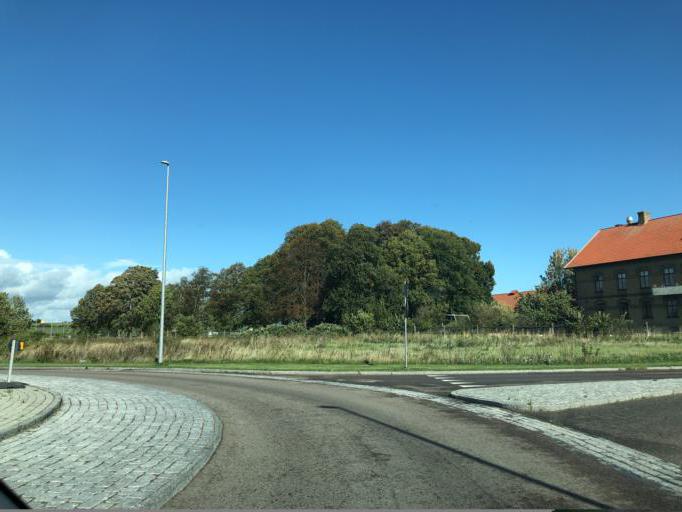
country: SE
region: Skane
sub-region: Landskrona
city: Landskrona
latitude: 55.9026
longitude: 12.8240
